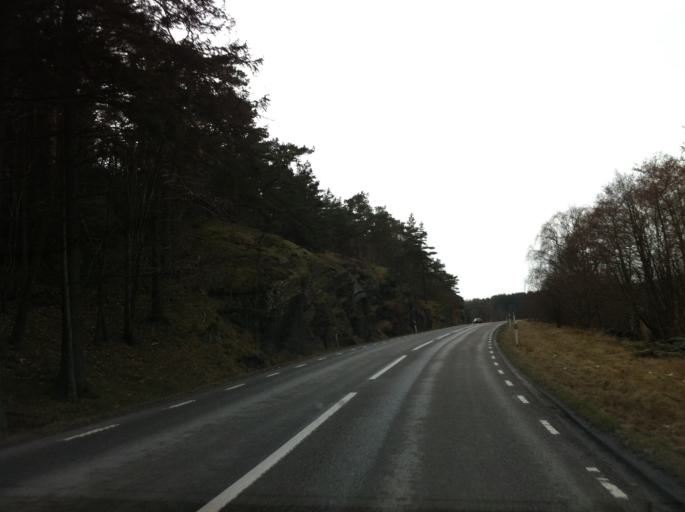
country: SE
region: Vaestra Goetaland
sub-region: Orust
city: Henan
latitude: 58.3094
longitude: 11.6976
